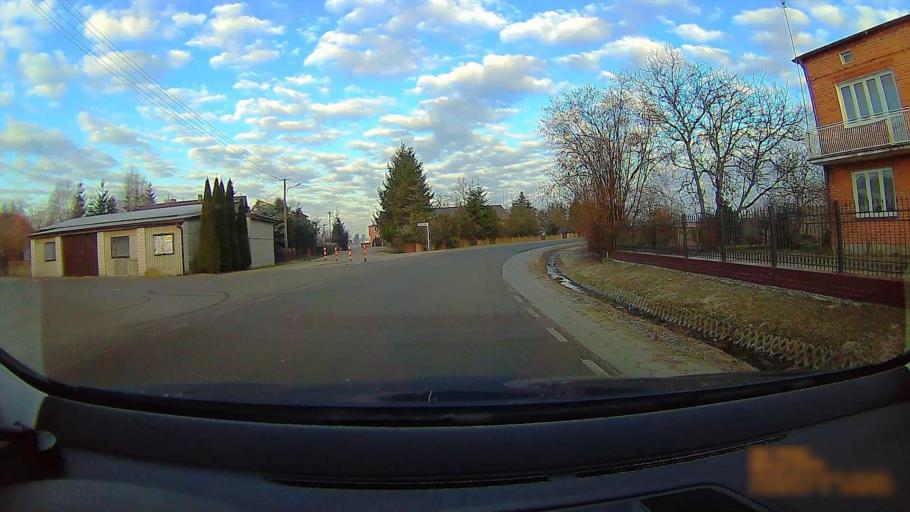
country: PL
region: Greater Poland Voivodeship
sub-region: Powiat koninski
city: Rzgow Pierwszy
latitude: 52.1045
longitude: 18.0876
